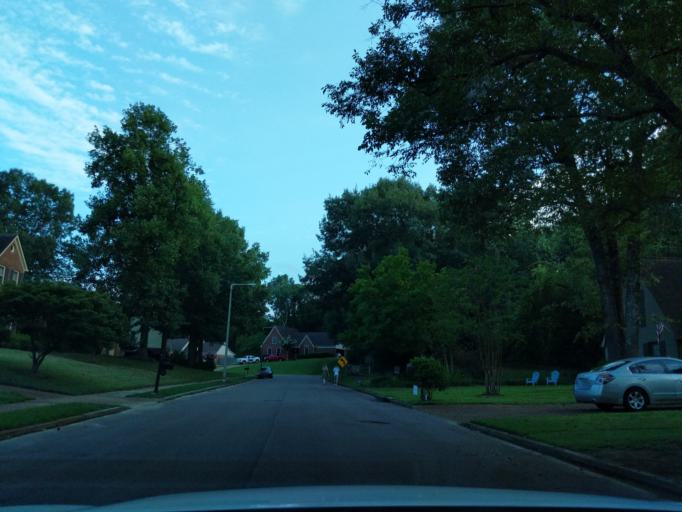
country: US
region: Tennessee
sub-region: Shelby County
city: Germantown
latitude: 35.0653
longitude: -89.7845
